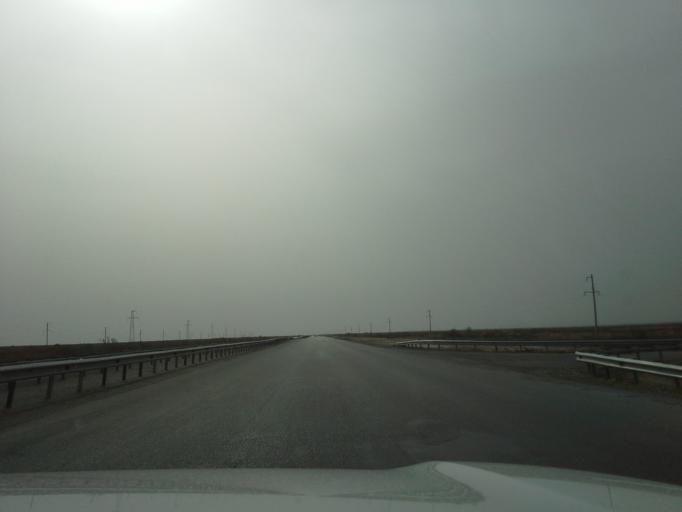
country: TM
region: Ahal
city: Kaka
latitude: 37.5126
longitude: 59.4391
